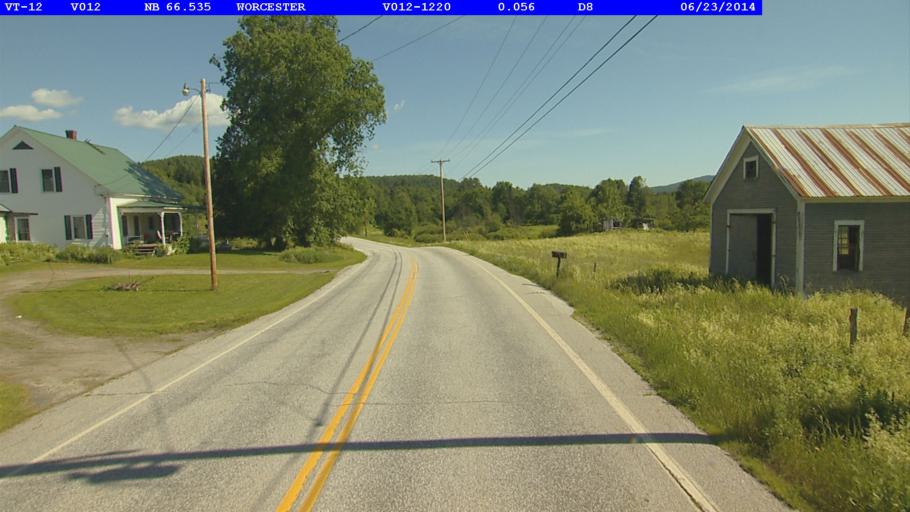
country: US
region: Vermont
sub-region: Washington County
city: Montpelier
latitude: 44.3535
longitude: -72.5647
